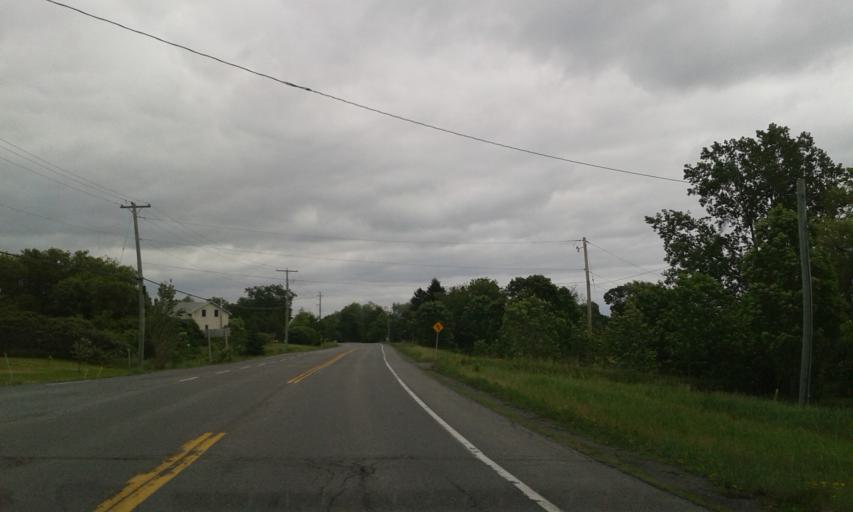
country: CA
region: Ontario
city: Skatepark
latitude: 44.1285
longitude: -76.8826
